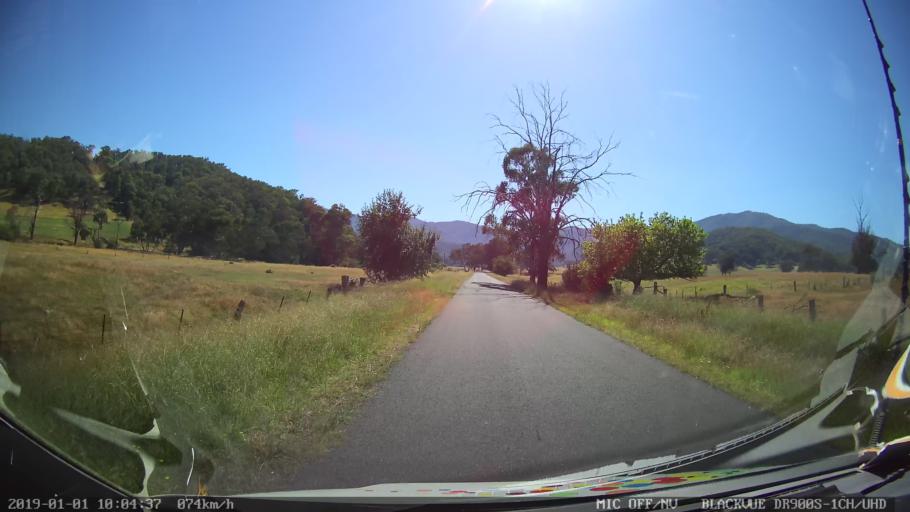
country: AU
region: New South Wales
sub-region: Snowy River
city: Jindabyne
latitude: -36.1754
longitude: 148.1248
